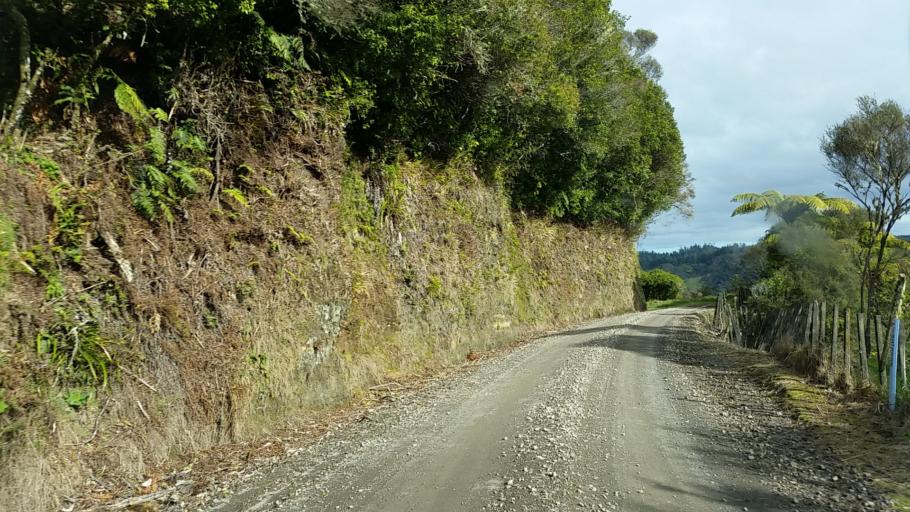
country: NZ
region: Taranaki
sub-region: South Taranaki District
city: Eltham
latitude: -39.1750
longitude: 174.6282
